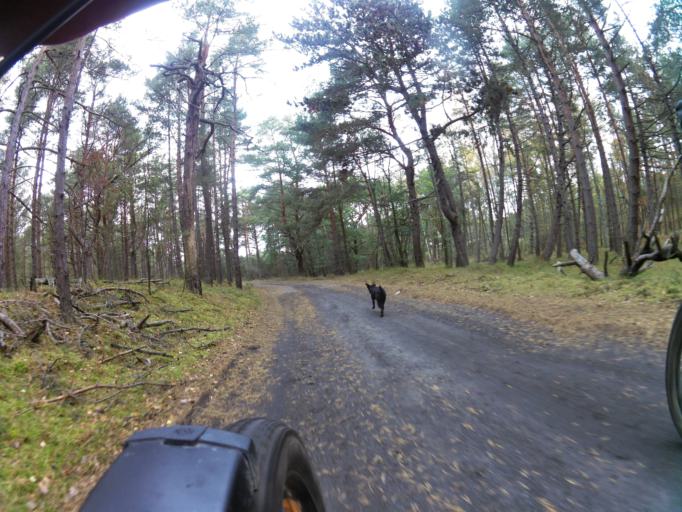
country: PL
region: Pomeranian Voivodeship
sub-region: Powiat pucki
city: Hel
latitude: 54.6212
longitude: 18.8201
